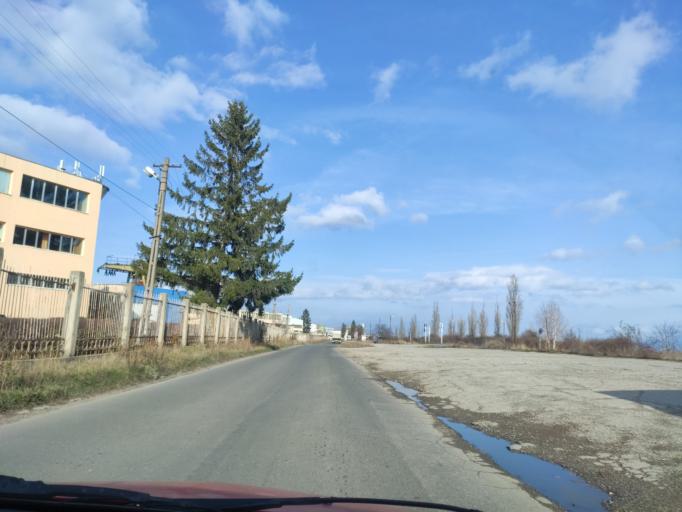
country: RO
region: Brasov
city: Codlea
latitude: 45.6893
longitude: 25.4567
